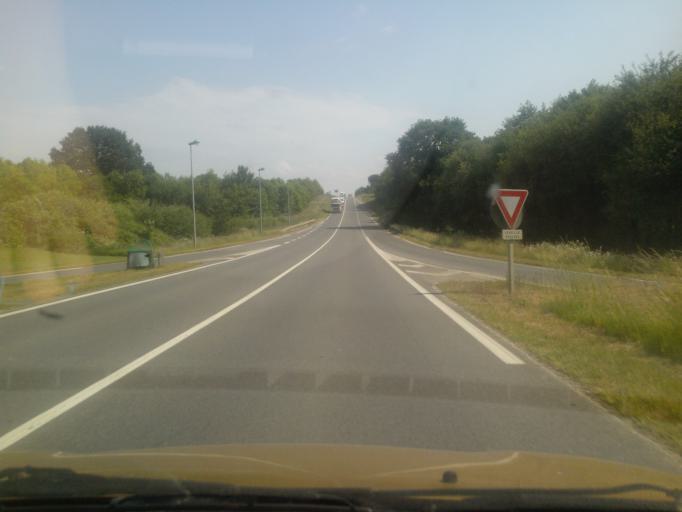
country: FR
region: Brittany
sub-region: Departement d'Ille-et-Vilaine
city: Melesse
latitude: 48.2123
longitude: -1.7005
